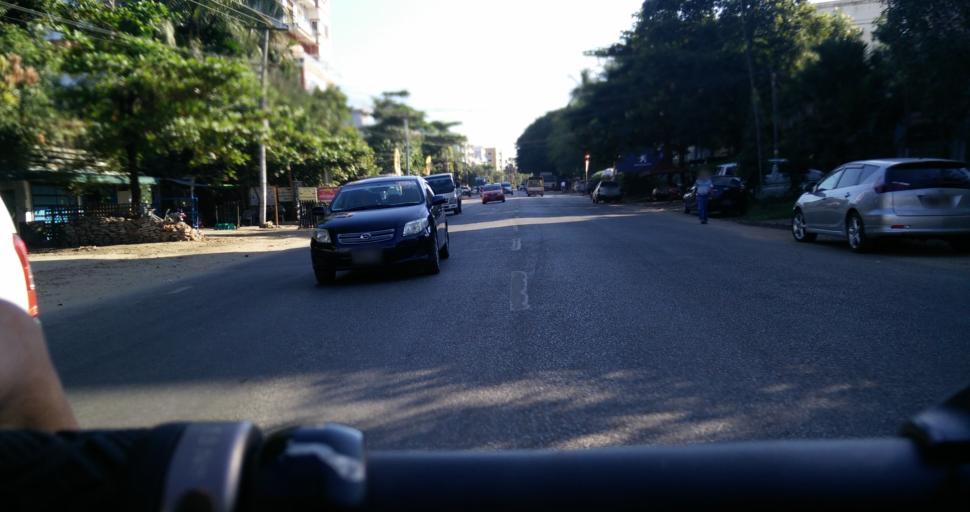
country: MM
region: Yangon
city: Yangon
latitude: 16.8372
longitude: 96.1867
